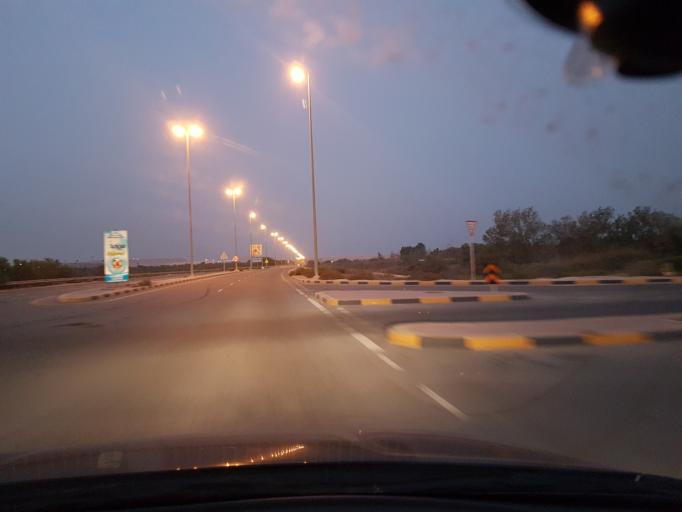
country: BH
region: Central Governorate
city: Dar Kulayb
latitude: 26.0189
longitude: 50.4939
